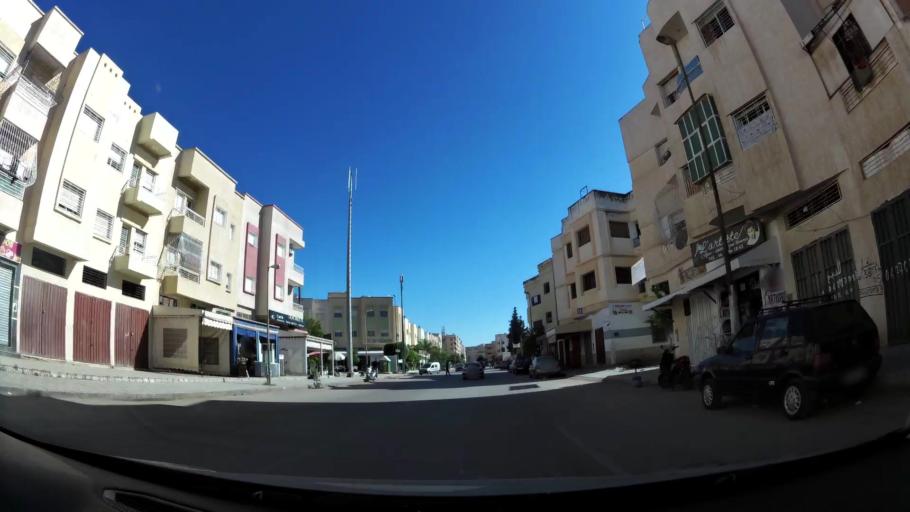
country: MA
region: Fes-Boulemane
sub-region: Fes
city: Fes
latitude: 34.0163
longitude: -4.9659
